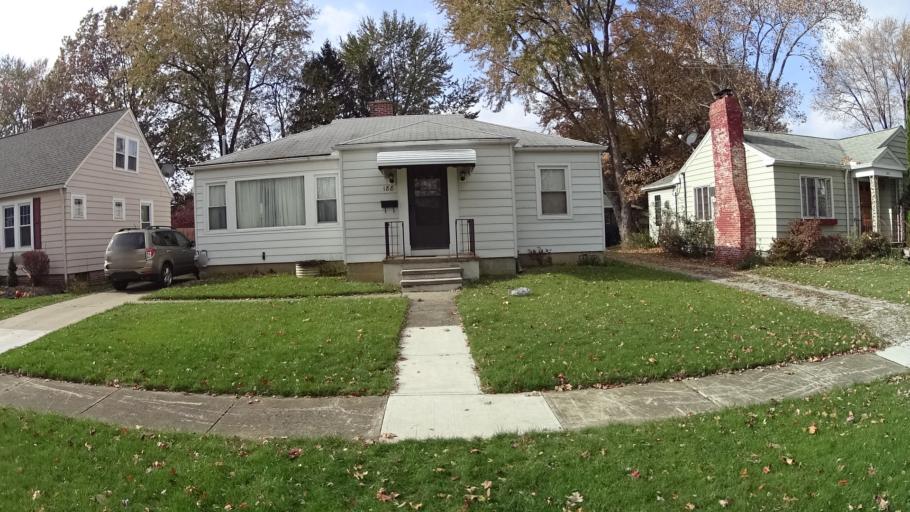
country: US
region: Ohio
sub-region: Lorain County
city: Elyria
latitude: 41.3778
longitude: -82.0893
